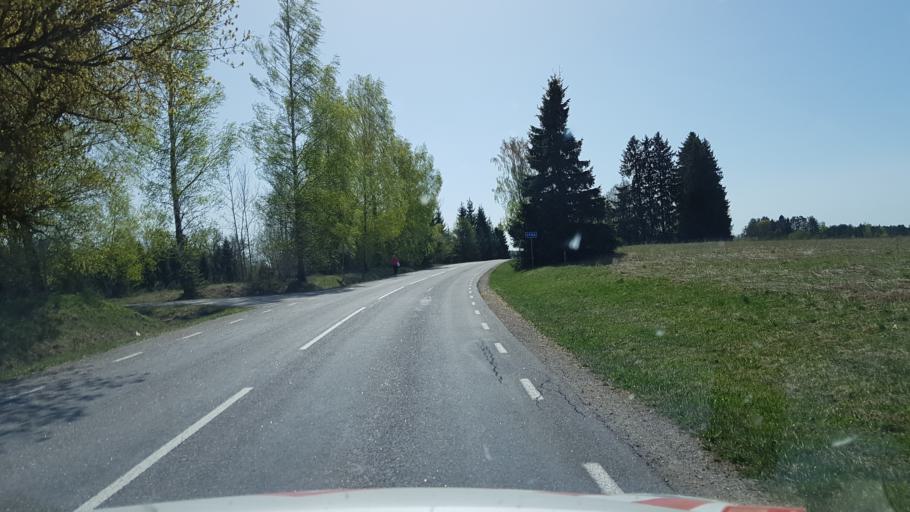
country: EE
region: Viljandimaa
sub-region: Suure-Jaani vald
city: Suure-Jaani
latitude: 58.5198
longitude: 25.4662
